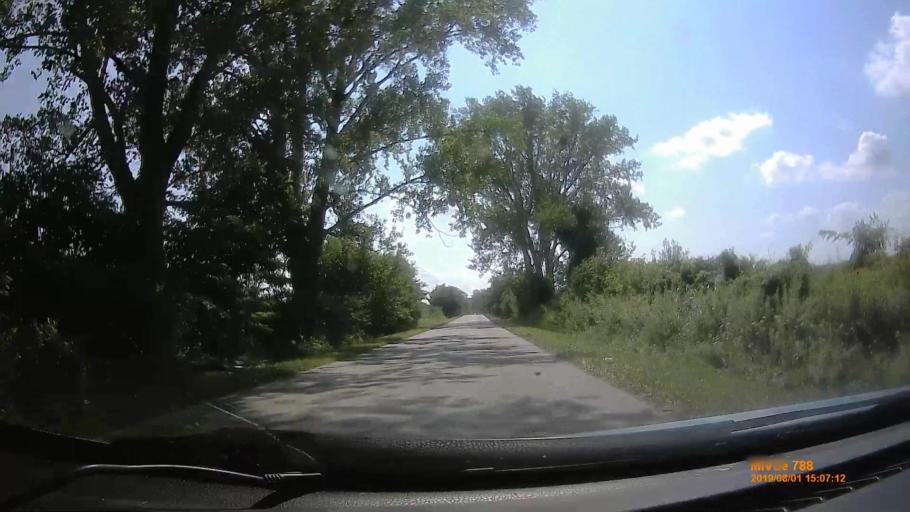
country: HU
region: Baranya
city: Sellye
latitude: 45.8608
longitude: 17.8324
